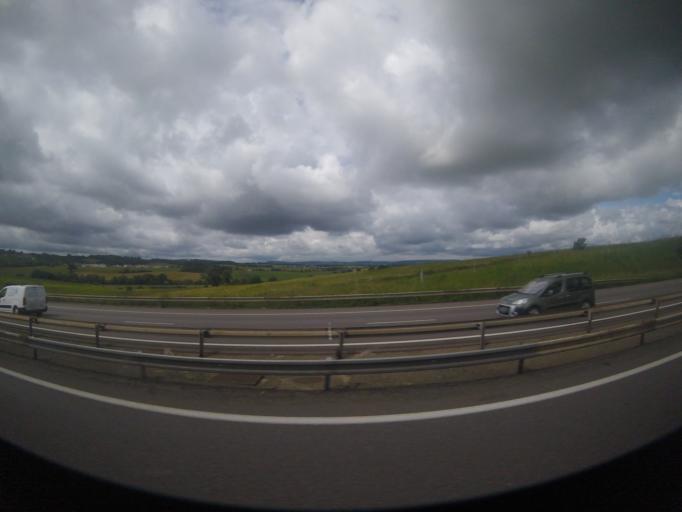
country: FR
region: Lorraine
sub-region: Departement de la Moselle
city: Saint-Julien-les-Metz
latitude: 49.1616
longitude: 6.2529
